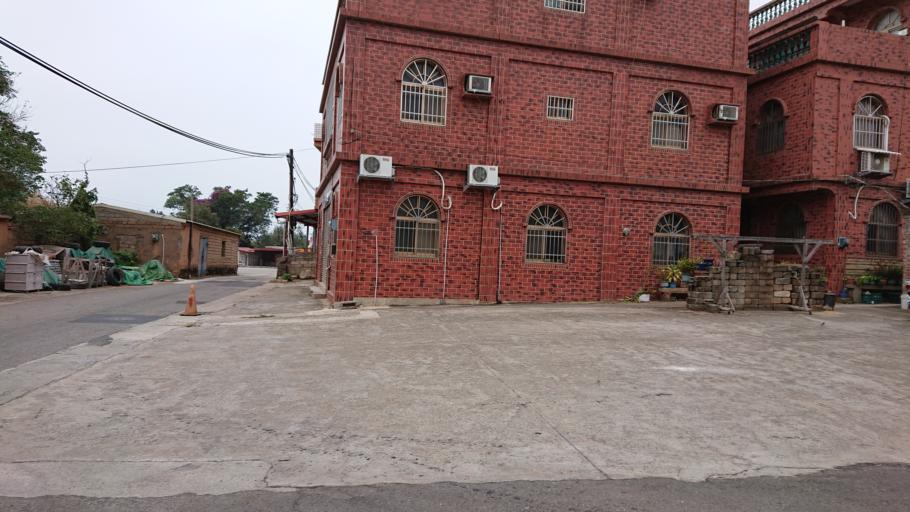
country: TW
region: Fukien
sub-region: Kinmen
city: Jincheng
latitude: 24.4473
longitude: 118.3157
